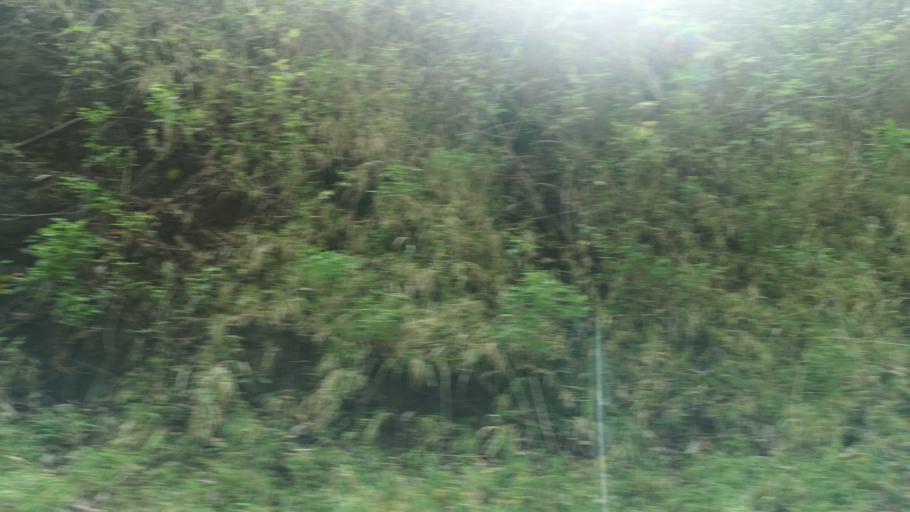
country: ES
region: Canary Islands
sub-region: Provincia de Santa Cruz de Tenerife
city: Hermigua
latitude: 28.1301
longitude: -17.2107
